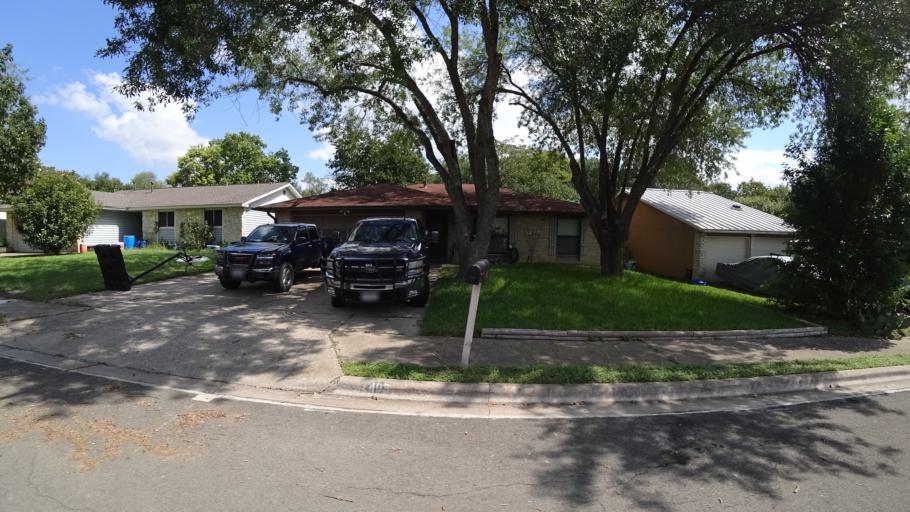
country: US
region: Texas
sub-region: Travis County
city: Onion Creek
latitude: 30.1871
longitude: -97.7878
